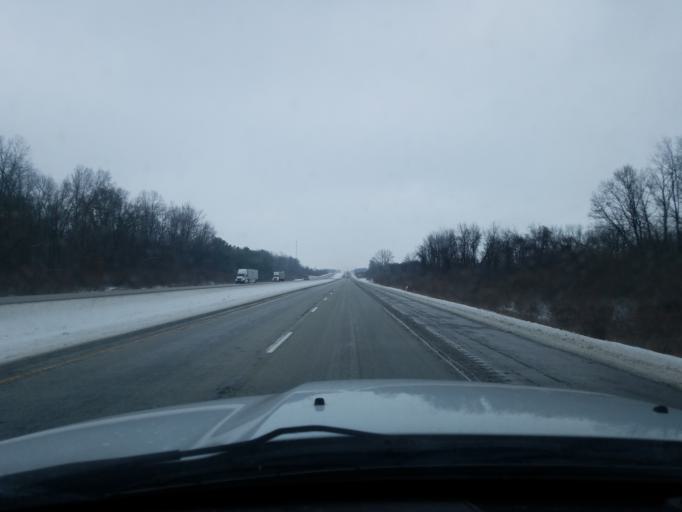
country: US
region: Indiana
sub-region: Fulton County
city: Rochester
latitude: 41.1308
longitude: -86.2397
